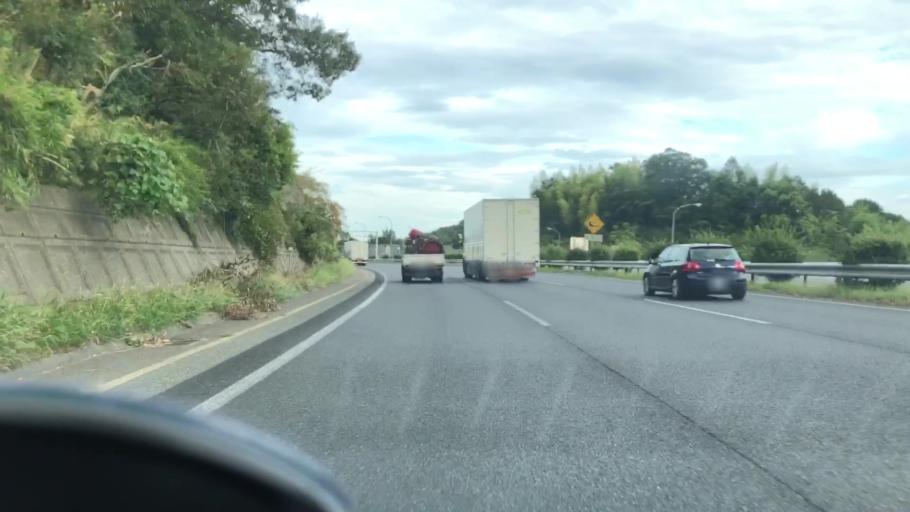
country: JP
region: Hyogo
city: Sandacho
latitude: 34.8856
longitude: 135.1645
